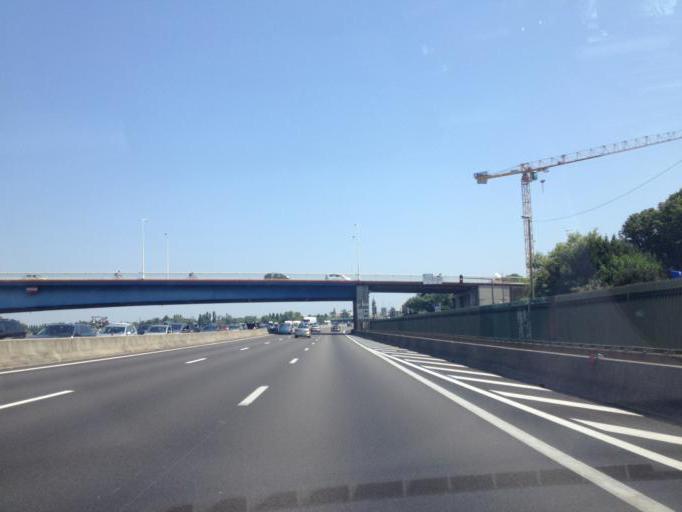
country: FR
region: Rhone-Alpes
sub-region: Departement de l'Ardeche
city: Guilherand-Granges
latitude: 44.9307
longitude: 4.8838
